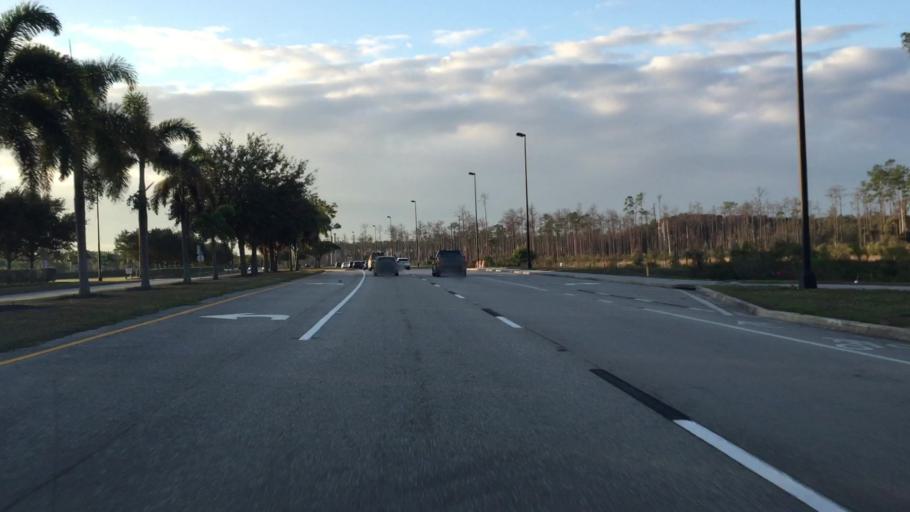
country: US
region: Florida
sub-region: Lee County
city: Three Oaks
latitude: 26.5051
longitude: -81.7856
